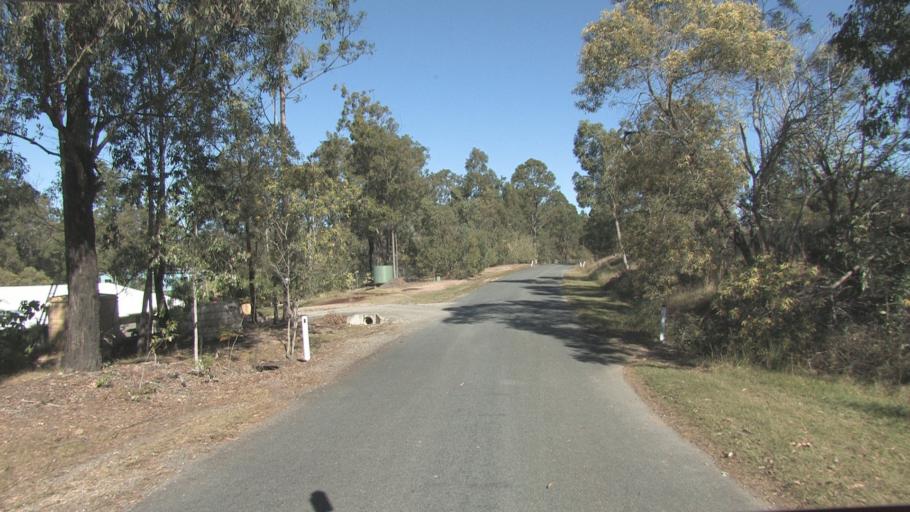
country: AU
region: Queensland
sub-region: Ipswich
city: Springfield Lakes
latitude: -27.7118
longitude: 152.9275
